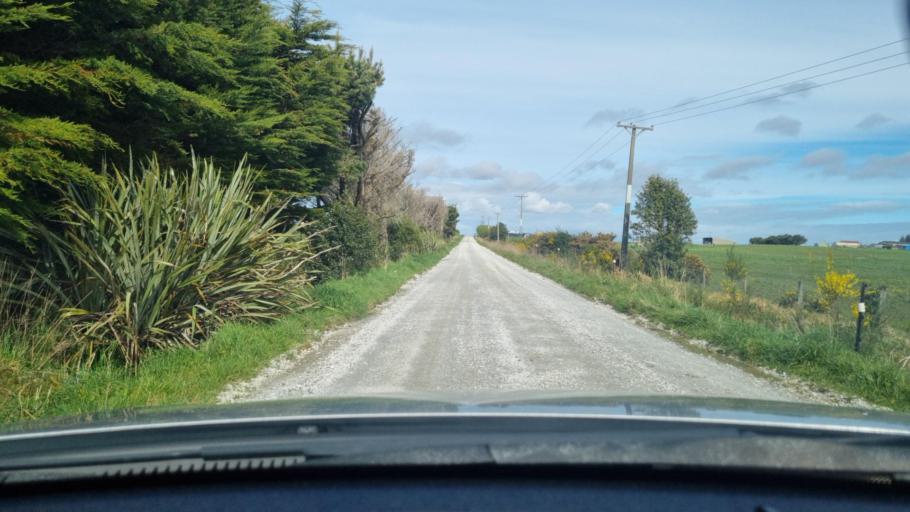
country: NZ
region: Southland
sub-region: Invercargill City
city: Invercargill
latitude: -46.4509
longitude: 168.3807
